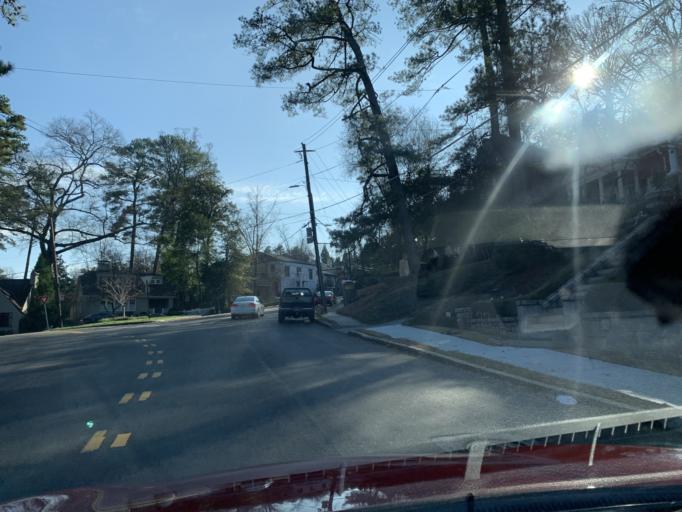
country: US
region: Georgia
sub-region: DeKalb County
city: Druid Hills
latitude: 33.7978
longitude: -84.3776
